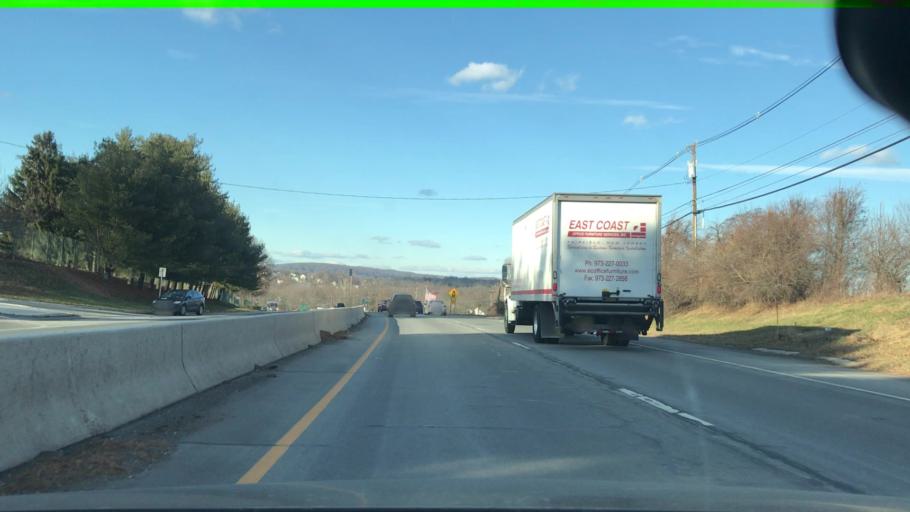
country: US
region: New Jersey
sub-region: Hunterdon County
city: Annandale
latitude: 40.6290
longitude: -74.8813
